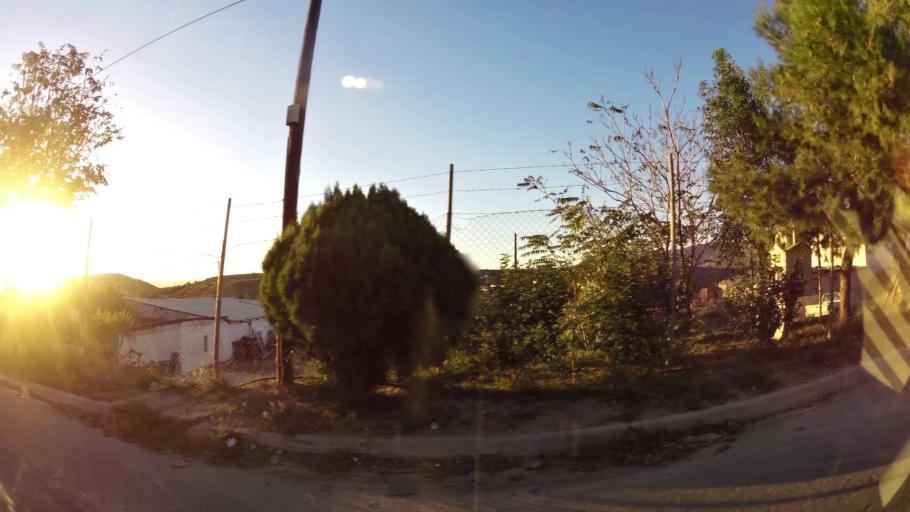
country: GR
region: Attica
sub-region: Nomarchia Athinas
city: Petroupolis
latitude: 38.0546
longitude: 23.6542
